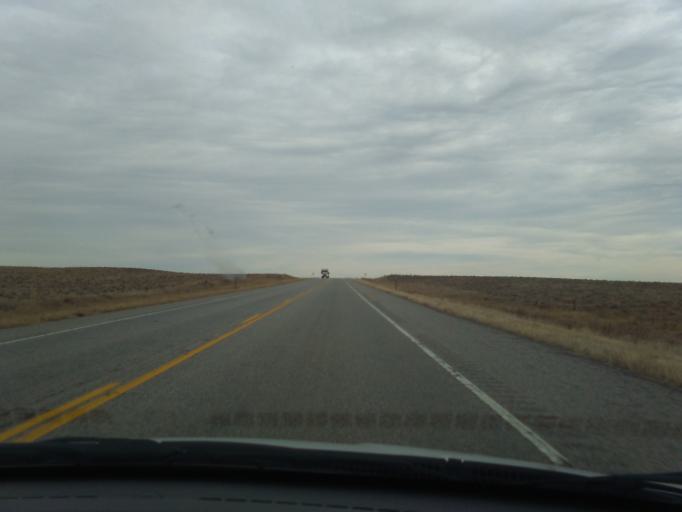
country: US
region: Colorado
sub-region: Morgan County
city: Brush
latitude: 40.2365
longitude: -103.4396
